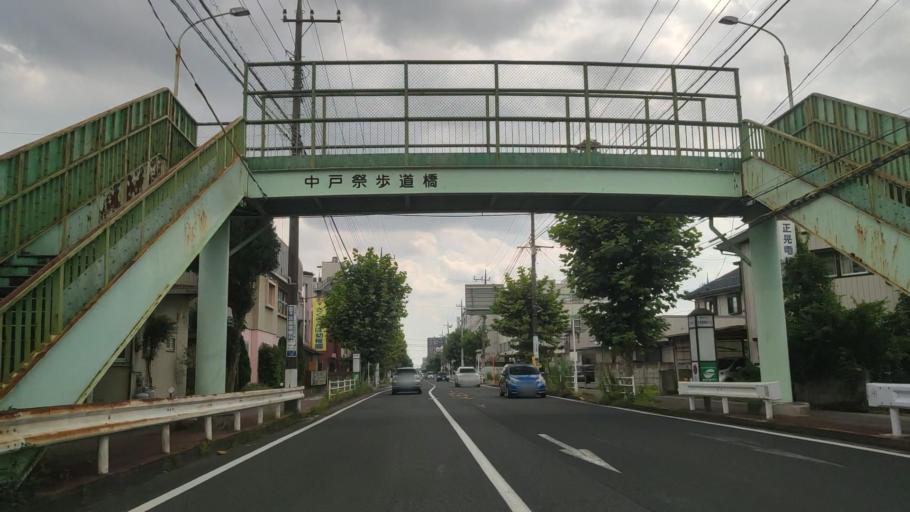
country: JP
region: Tochigi
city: Utsunomiya-shi
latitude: 36.5735
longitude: 139.8706
